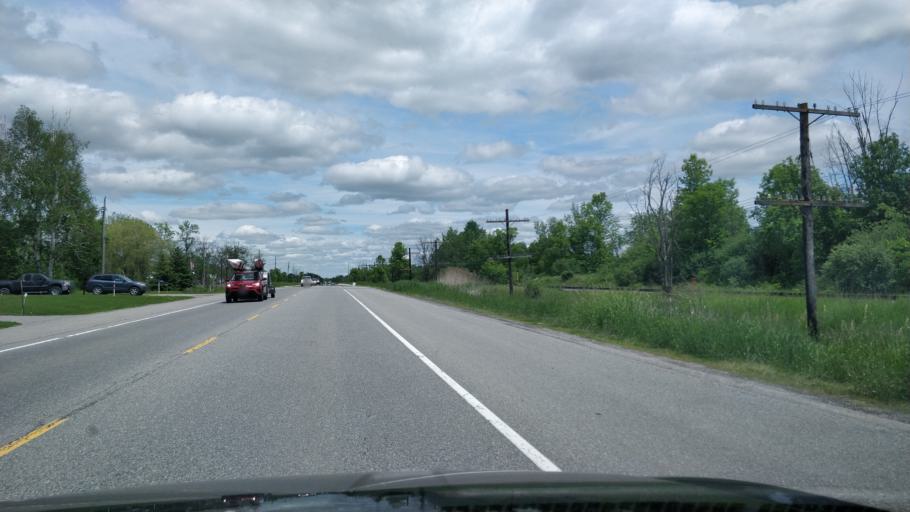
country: CA
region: Ontario
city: Perth
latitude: 44.8891
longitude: -76.3042
